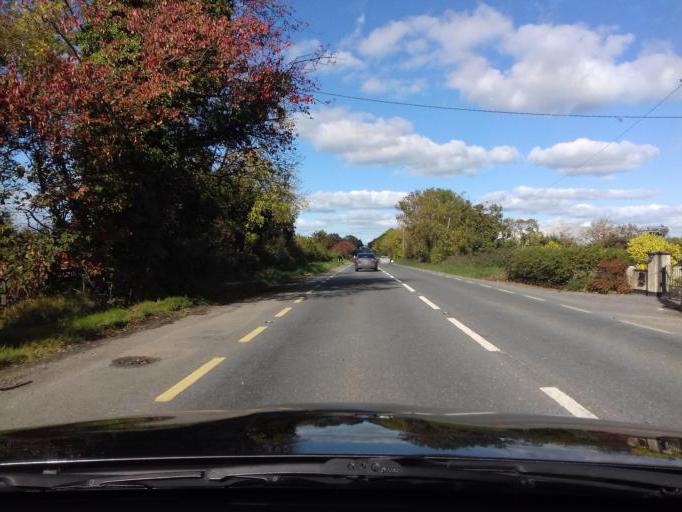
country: IE
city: Kentstown
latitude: 53.6602
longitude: -6.5255
